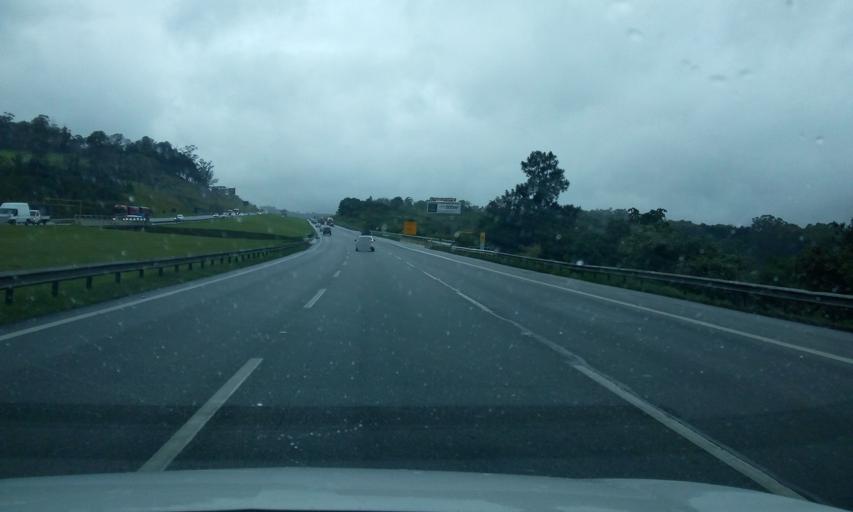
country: BR
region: Sao Paulo
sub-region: Jundiai
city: Jundiai
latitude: -23.2478
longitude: -46.8789
